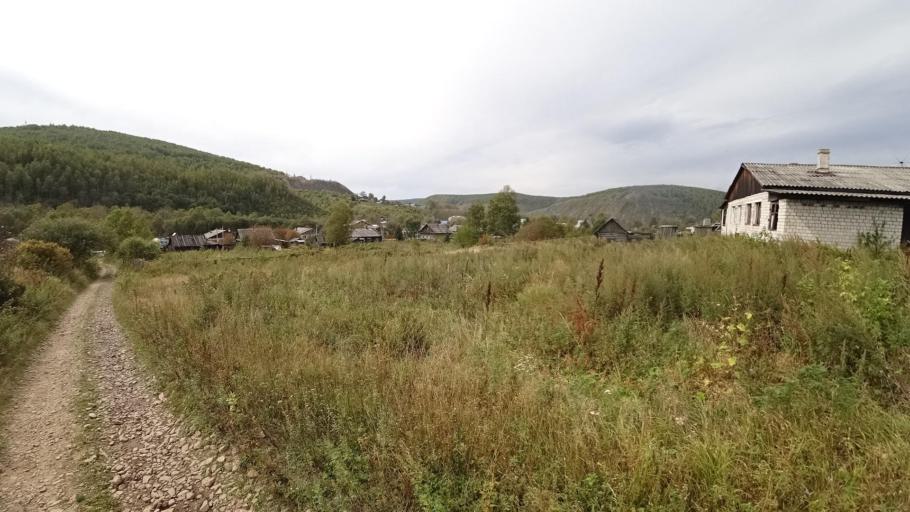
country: RU
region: Jewish Autonomous Oblast
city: Khingansk
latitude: 49.1222
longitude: 131.2076
